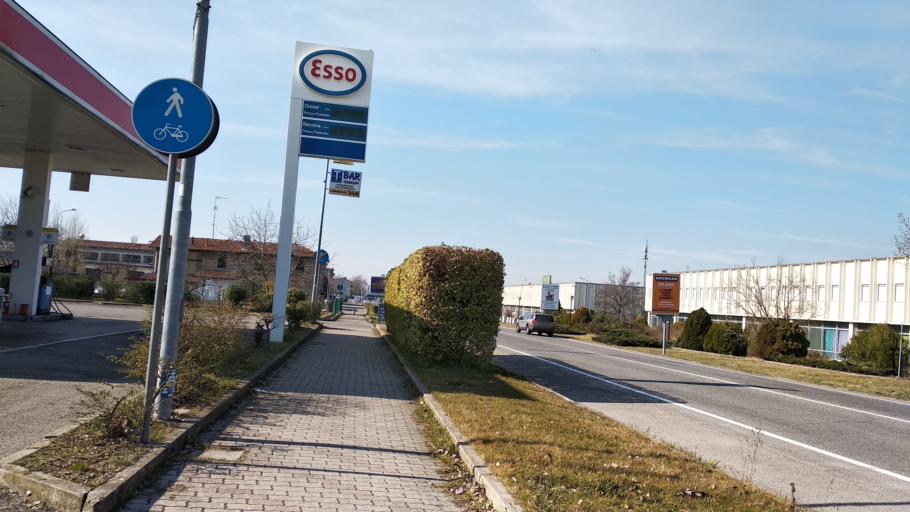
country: IT
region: Emilia-Romagna
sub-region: Provincia di Bologna
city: Ozzano dell'Emilia
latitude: 44.4419
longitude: 11.4839
